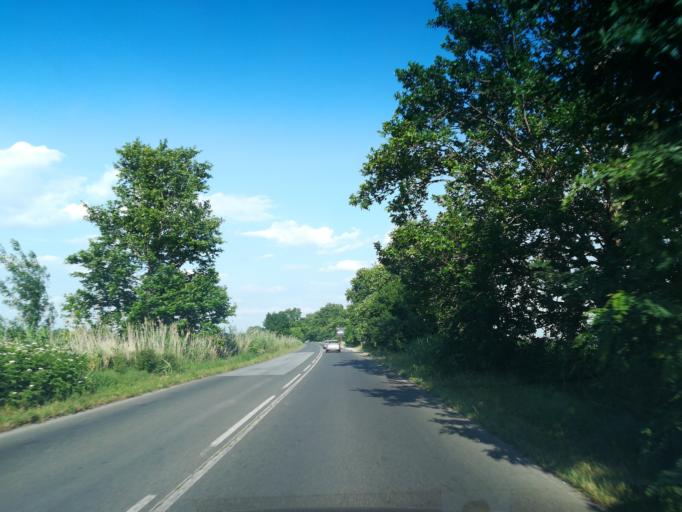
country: BG
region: Plovdiv
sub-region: Obshtina Sadovo
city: Sadovo
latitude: 42.1465
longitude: 24.8450
